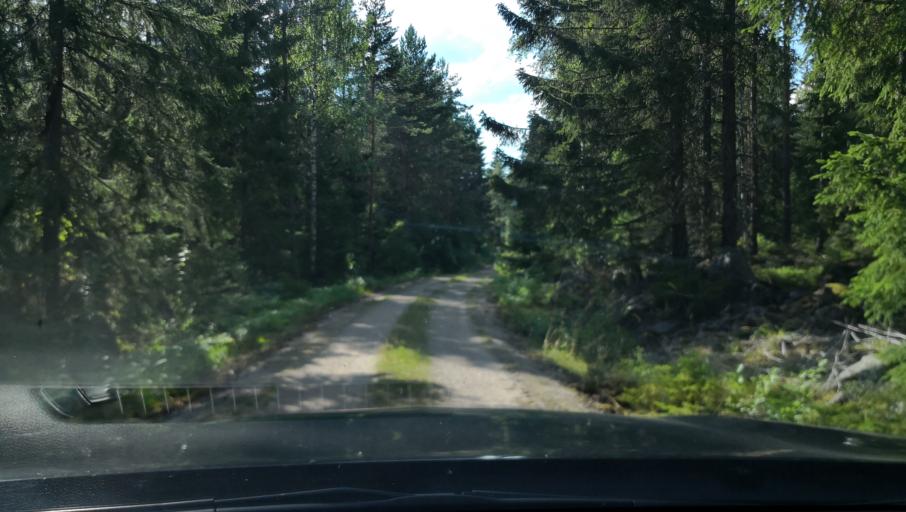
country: SE
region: Vaestmanland
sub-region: Vasteras
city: Skultuna
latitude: 59.7231
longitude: 16.3309
